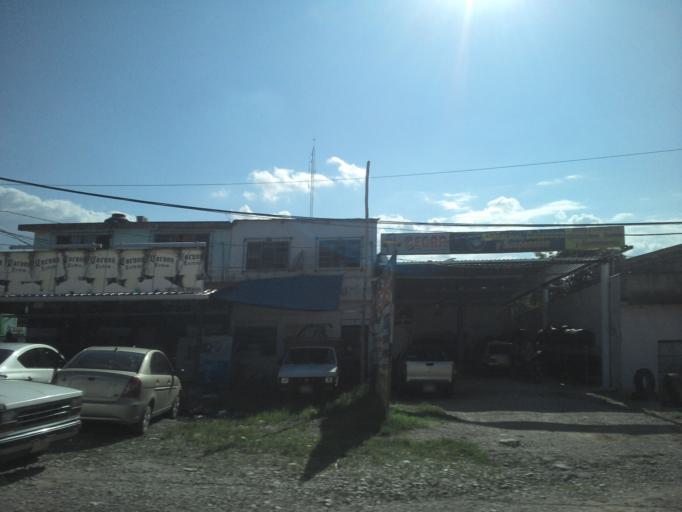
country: MX
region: Chiapas
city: Palenque
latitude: 17.5502
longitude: -91.9855
